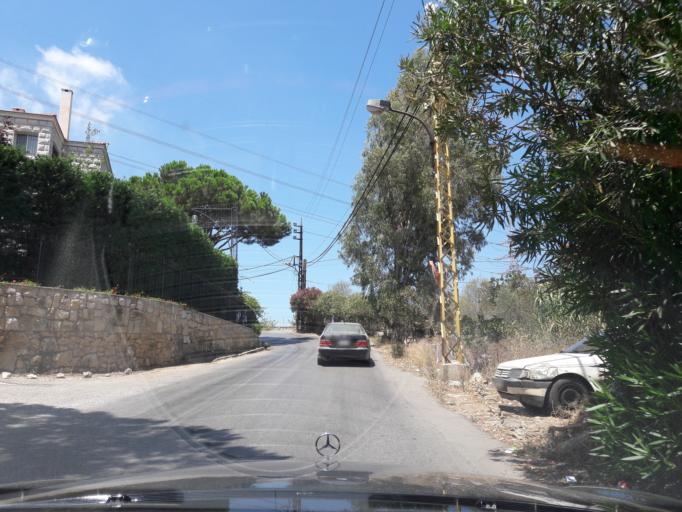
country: LB
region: Mont-Liban
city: Djounie
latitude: 33.9257
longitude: 35.6554
